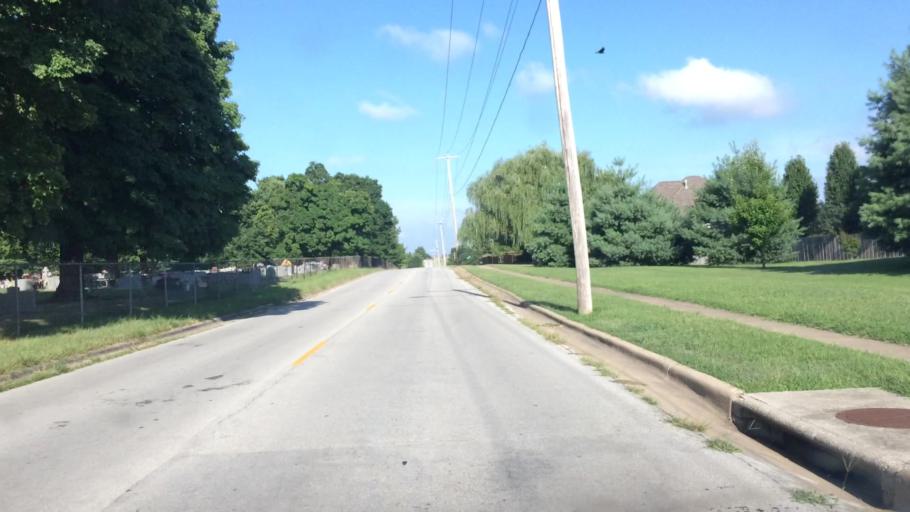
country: US
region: Missouri
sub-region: Greene County
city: Springfield
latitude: 37.2661
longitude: -93.2733
